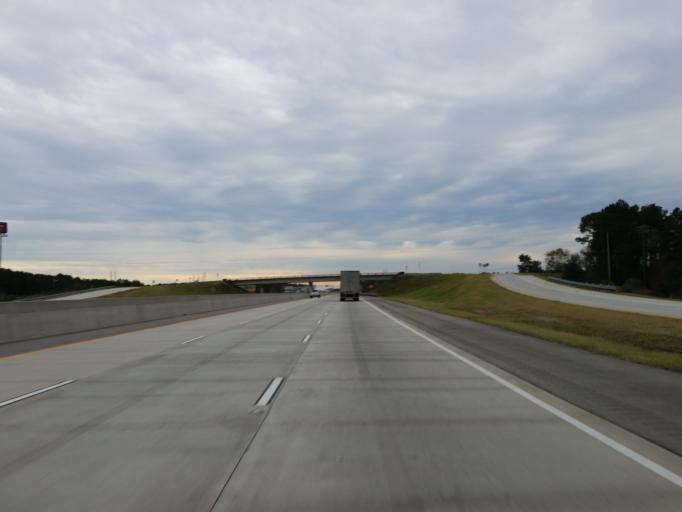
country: US
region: Georgia
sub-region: Cook County
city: Sparks
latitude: 31.2173
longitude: -83.4604
